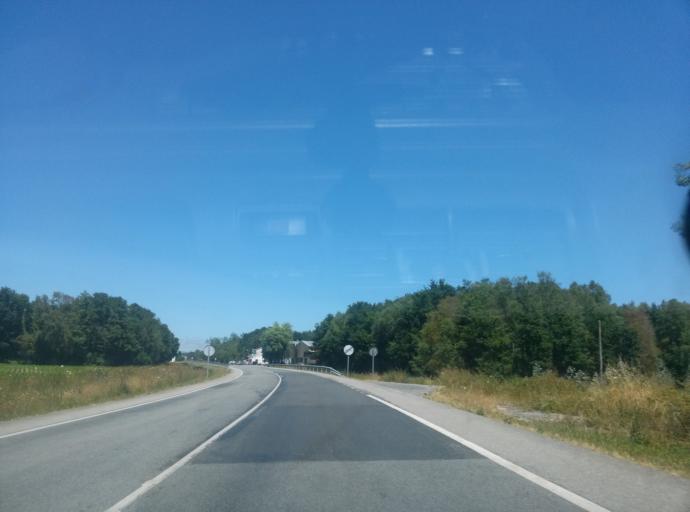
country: ES
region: Galicia
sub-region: Provincia de Lugo
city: Castro de Rei
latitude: 43.1844
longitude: -7.4736
